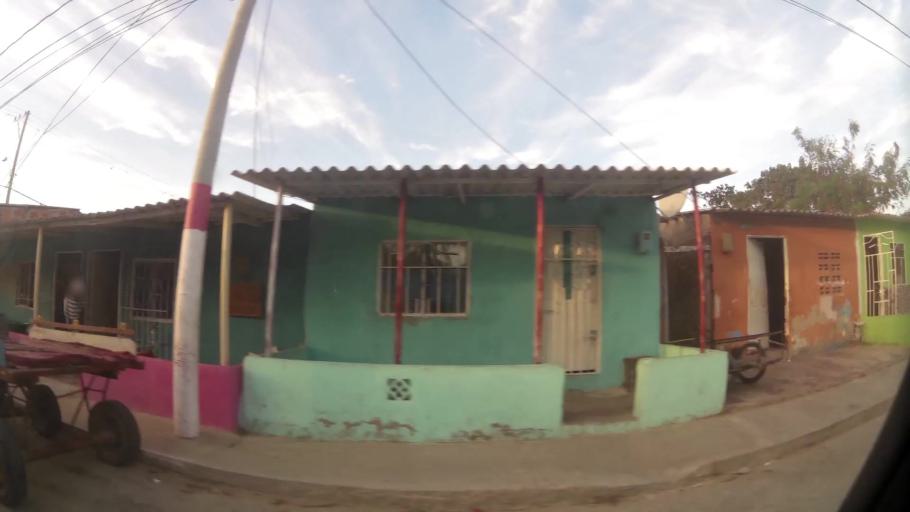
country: CO
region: Atlantico
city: Barranquilla
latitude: 10.9528
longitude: -74.8267
